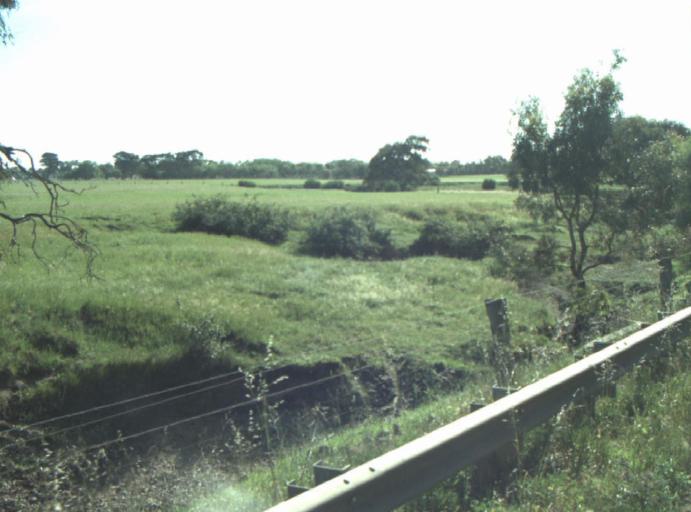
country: AU
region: Victoria
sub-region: Greater Geelong
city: Lara
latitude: -38.0070
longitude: 144.3838
